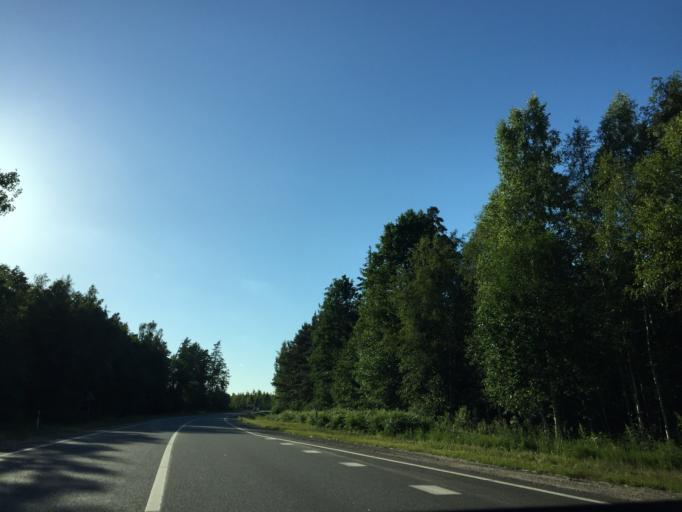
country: LV
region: Ventspils
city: Ventspils
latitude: 57.3788
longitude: 21.7164
